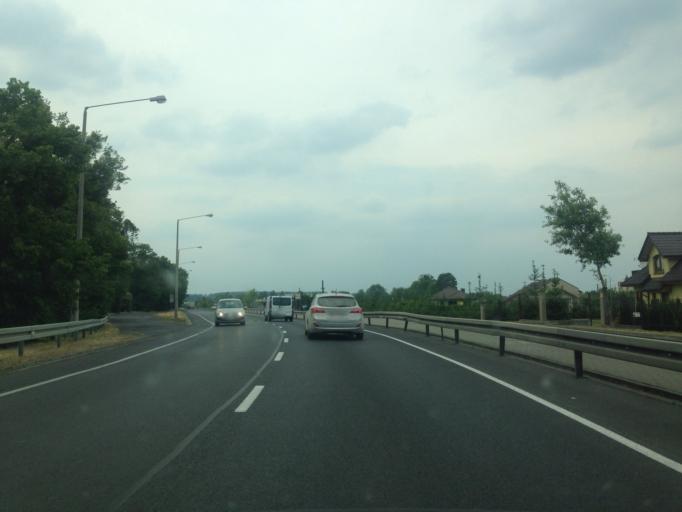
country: PL
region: Kujawsko-Pomorskie
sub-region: Grudziadz
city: Grudziadz
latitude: 53.5045
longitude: 18.8386
